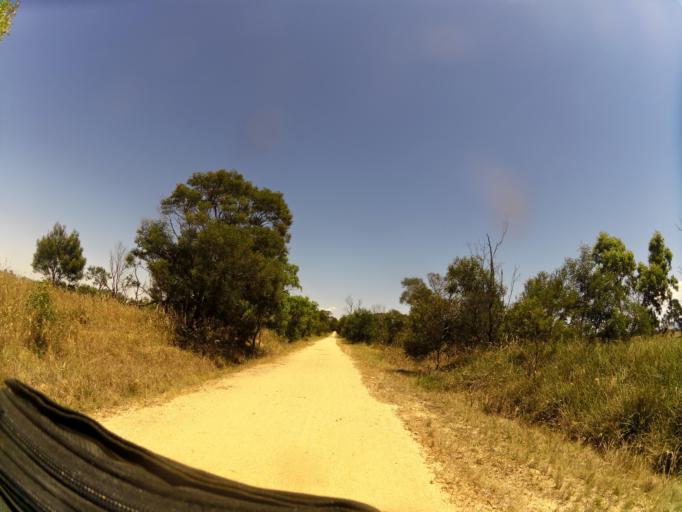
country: AU
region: Victoria
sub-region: Wellington
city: Sale
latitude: -37.9746
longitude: 147.0070
